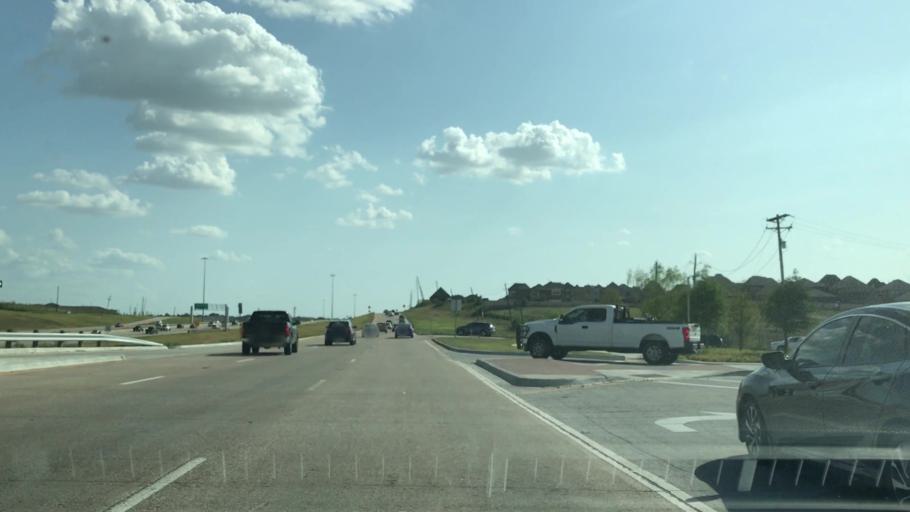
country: US
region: Texas
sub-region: Dallas County
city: Irving
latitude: 32.8783
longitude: -96.9921
